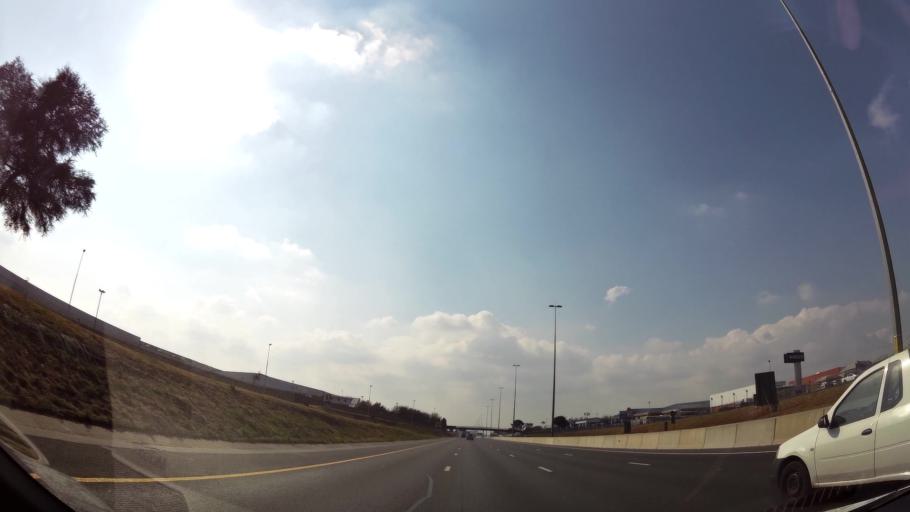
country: ZA
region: Gauteng
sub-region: Ekurhuleni Metropolitan Municipality
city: Boksburg
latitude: -26.1795
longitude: 28.2156
